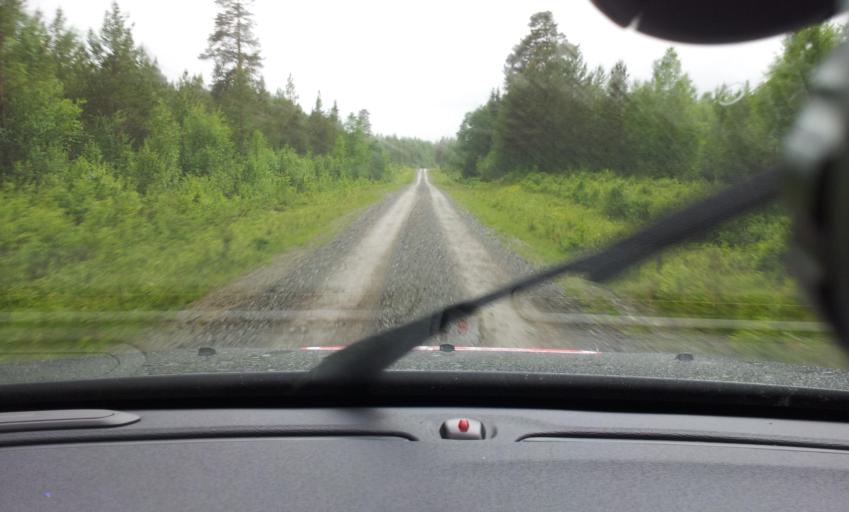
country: SE
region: Jaemtland
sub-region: Are Kommun
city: Are
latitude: 63.1842
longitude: 13.1481
